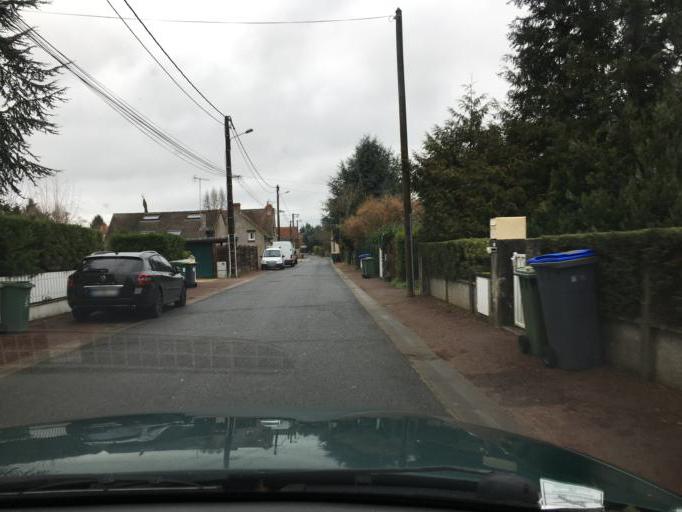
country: FR
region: Centre
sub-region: Departement du Loiret
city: Saint-Pryve-Saint-Mesmin
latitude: 47.8637
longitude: 1.8757
